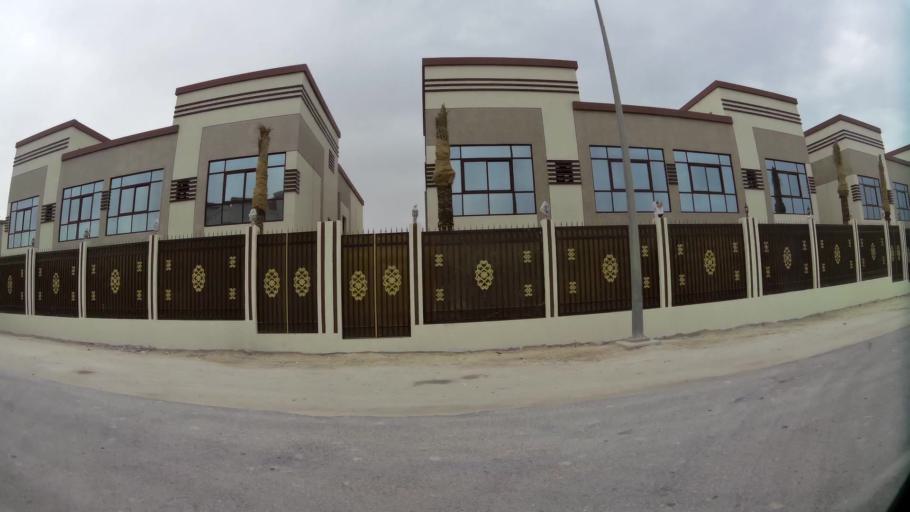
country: QA
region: Baladiyat ar Rayyan
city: Ar Rayyan
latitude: 25.3391
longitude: 51.4619
